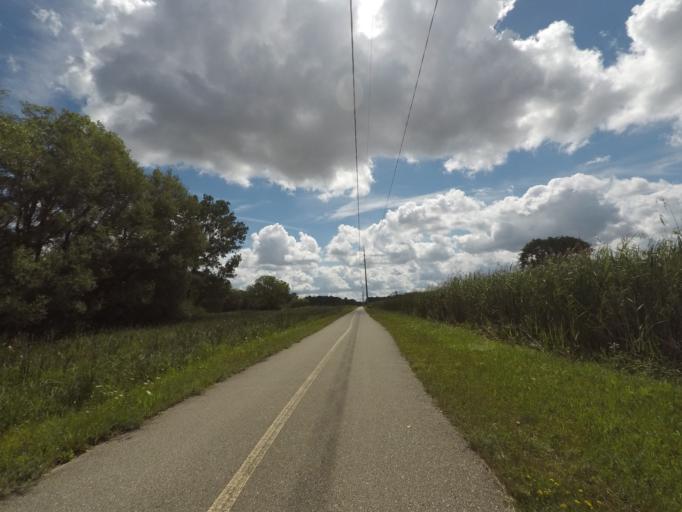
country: US
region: Wisconsin
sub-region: Waukesha County
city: Pewaukee
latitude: 43.0556
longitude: -88.2889
